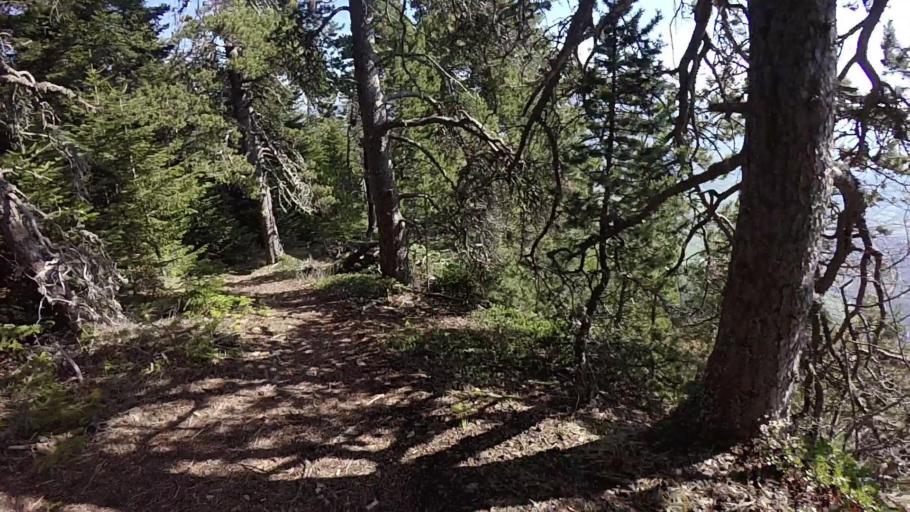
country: FR
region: Provence-Alpes-Cote d'Azur
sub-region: Departement des Alpes-de-Haute-Provence
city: Seyne-les-Alpes
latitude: 44.3417
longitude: 6.3028
